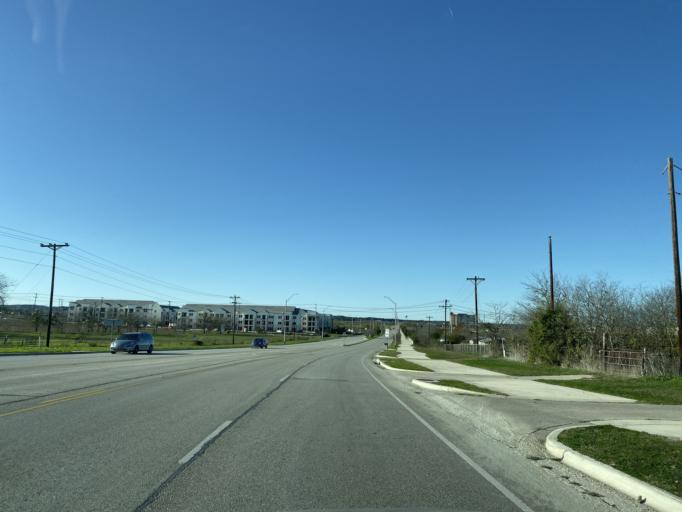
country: US
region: Texas
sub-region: Guadalupe County
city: Redwood
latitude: 29.8288
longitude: -97.9594
